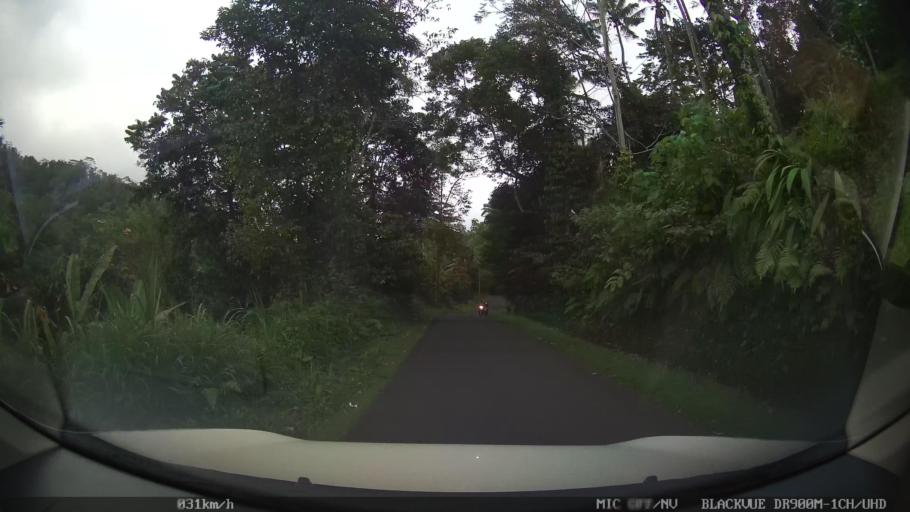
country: ID
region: Bali
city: Peneng
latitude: -8.3646
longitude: 115.2205
